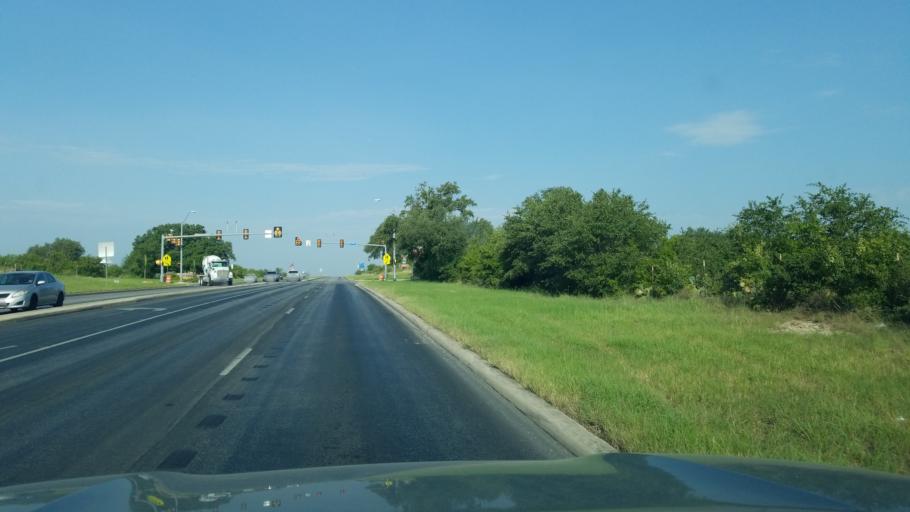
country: US
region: Texas
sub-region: Bexar County
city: Leon Valley
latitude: 29.4622
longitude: -98.7289
